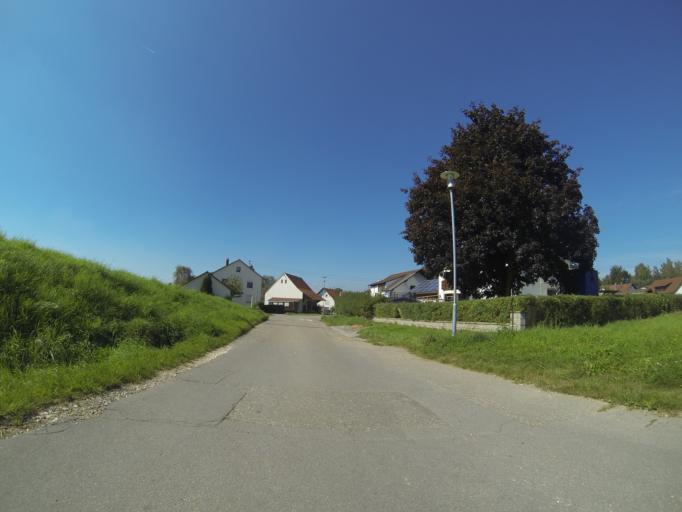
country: DE
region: Baden-Wuerttemberg
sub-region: Tuebingen Region
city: Achstetten
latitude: 48.2754
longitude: 9.9090
